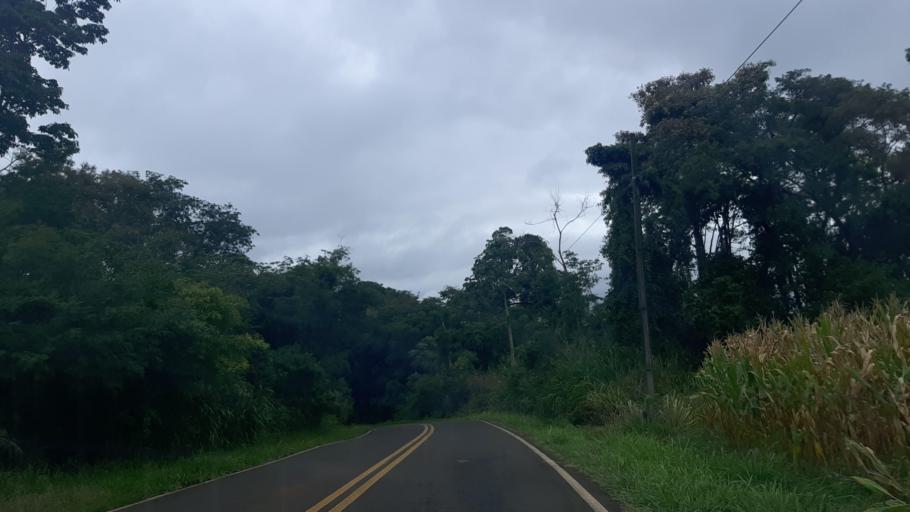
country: BR
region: Parana
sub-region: Ampere
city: Ampere
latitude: -25.9664
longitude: -53.4435
